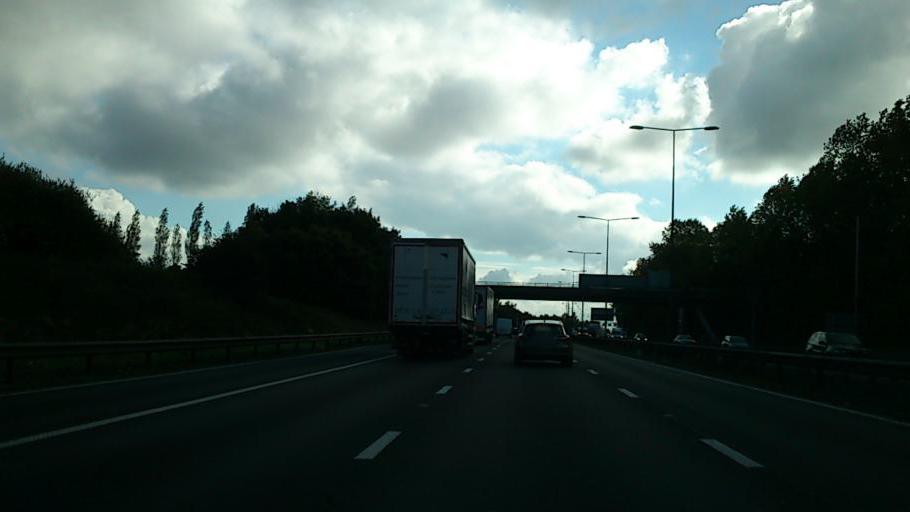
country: GB
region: England
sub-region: Staffordshire
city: Essington
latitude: 52.6244
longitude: -2.0405
